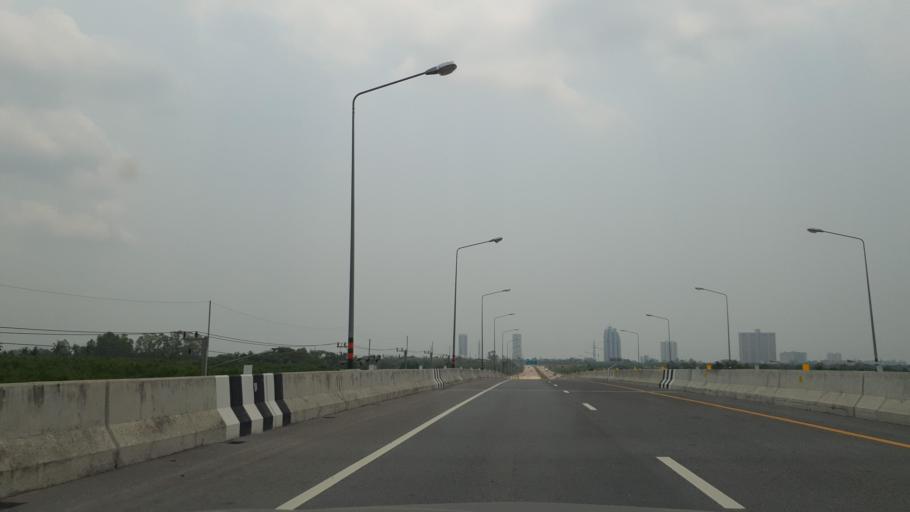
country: TH
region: Chon Buri
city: Phatthaya
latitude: 12.8368
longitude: 100.9364
